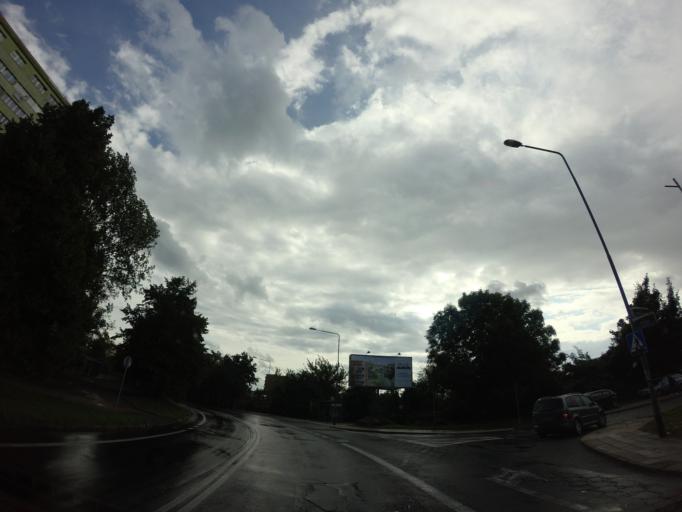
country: PL
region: West Pomeranian Voivodeship
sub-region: Szczecin
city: Szczecin
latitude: 53.4488
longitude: 14.5616
